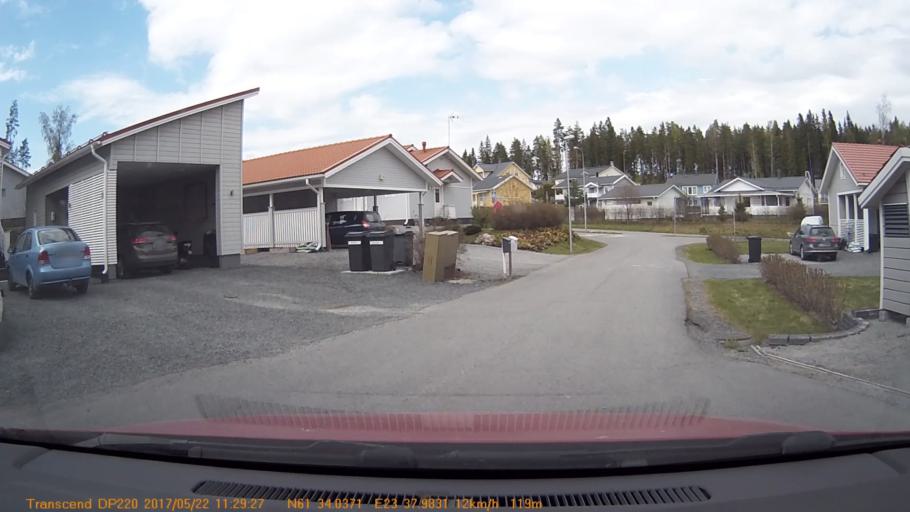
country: FI
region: Pirkanmaa
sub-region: Tampere
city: Yloejaervi
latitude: 61.5673
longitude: 23.6330
